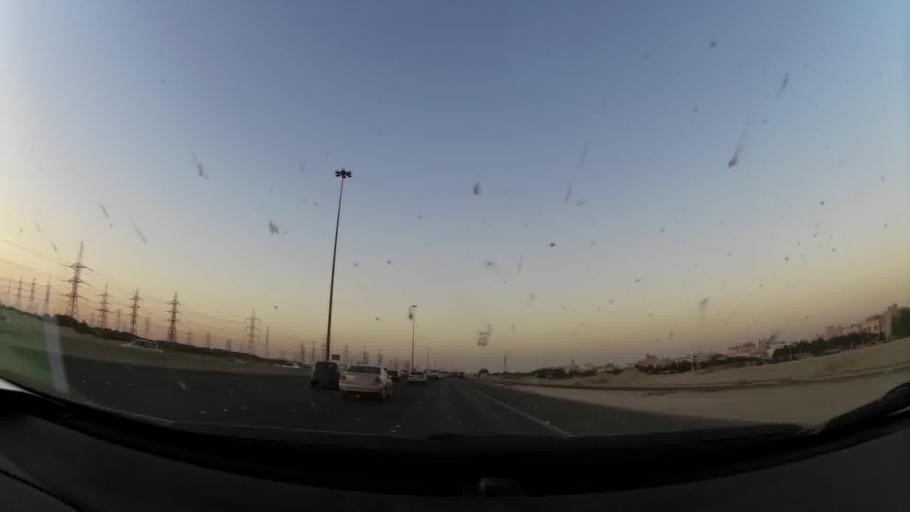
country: KW
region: Mubarak al Kabir
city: Mubarak al Kabir
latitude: 29.1789
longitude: 48.0679
